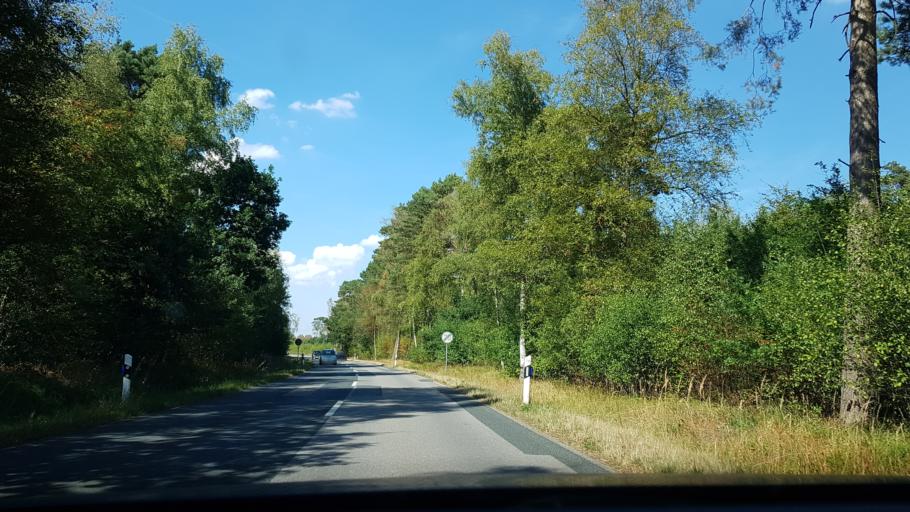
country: DE
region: Lower Saxony
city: Isenbuttel
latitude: 52.4456
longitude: 10.6083
